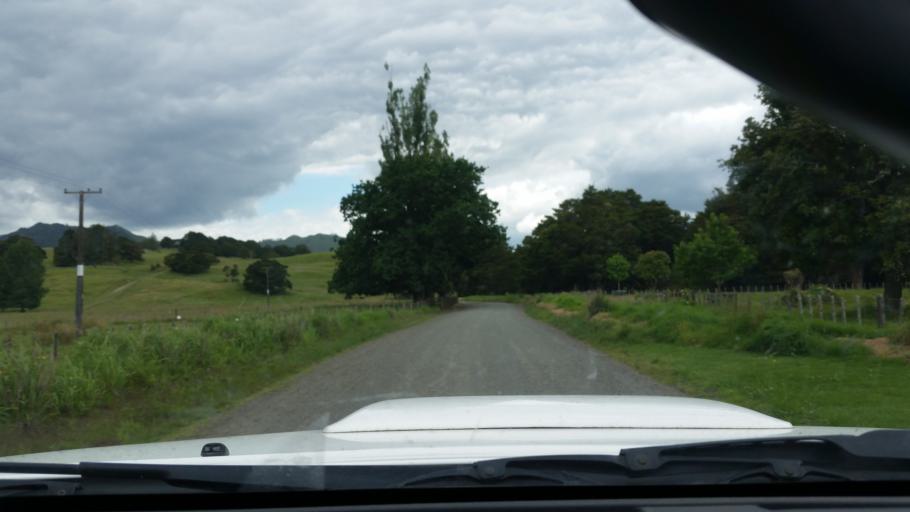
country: NZ
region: Northland
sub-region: Kaipara District
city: Dargaville
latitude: -35.8136
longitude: 173.8956
